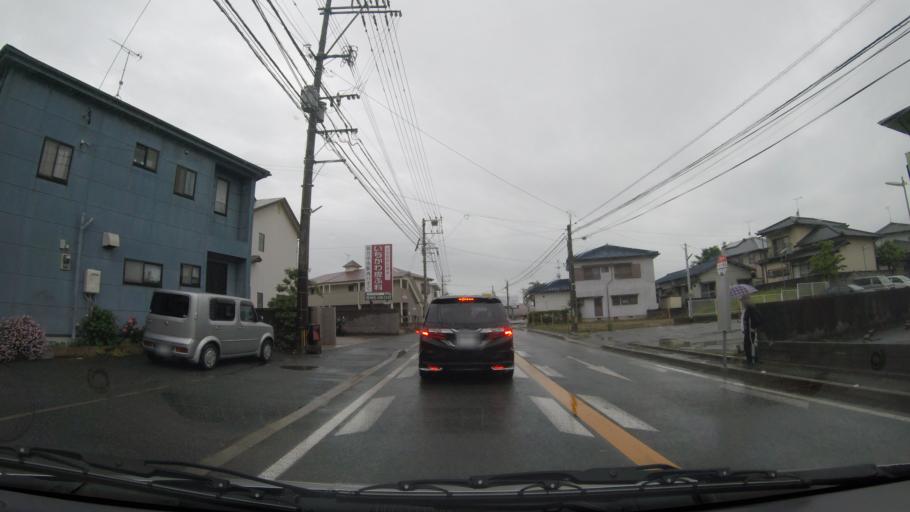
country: JP
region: Fukuoka
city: Koga
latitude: 33.7241
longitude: 130.4579
